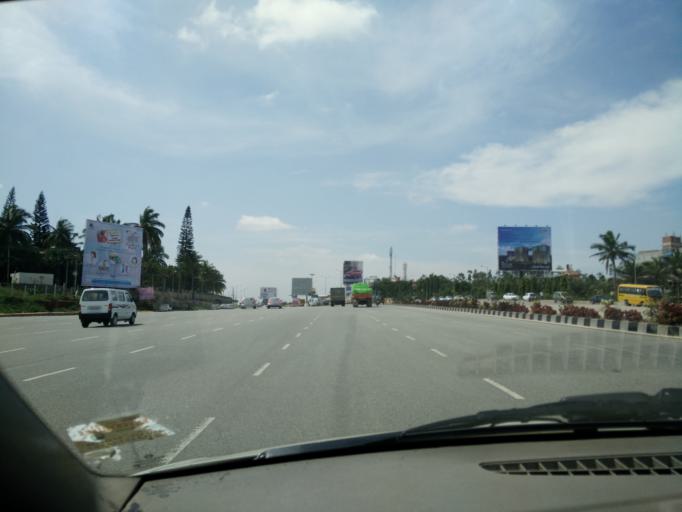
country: IN
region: Karnataka
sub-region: Bangalore Rural
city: Devanhalli
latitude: 13.1925
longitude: 77.6484
